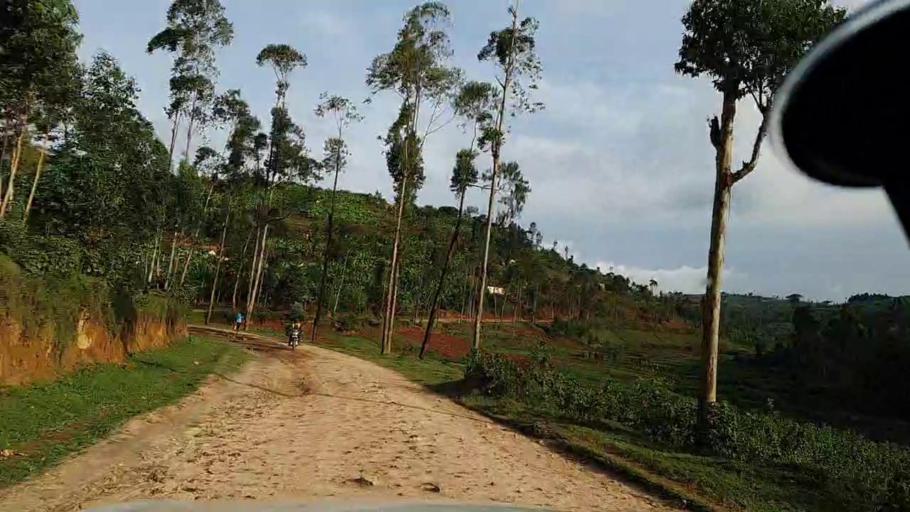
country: RW
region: Southern Province
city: Gitarama
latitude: -2.1761
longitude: 29.5571
